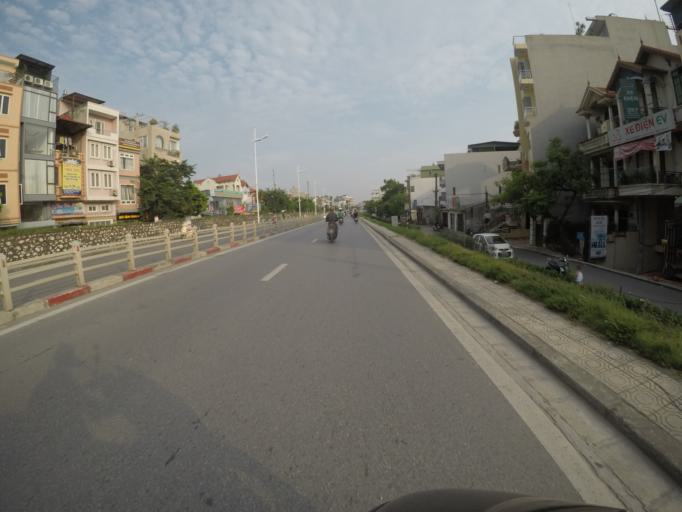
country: VN
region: Ha Noi
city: Tay Ho
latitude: 21.0747
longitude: 105.8235
